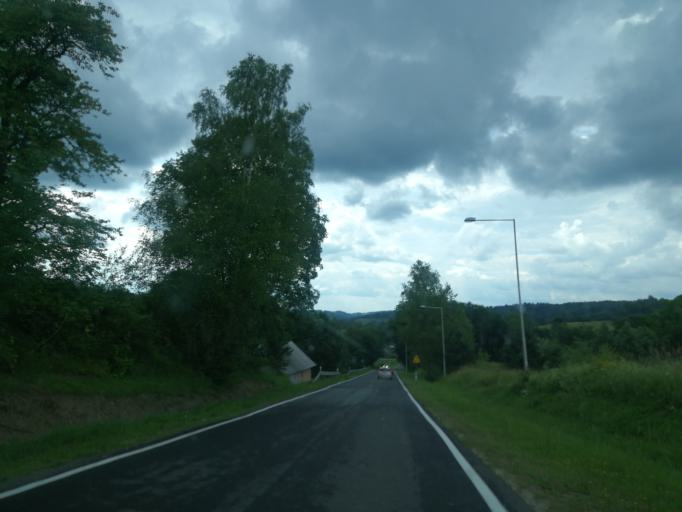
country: PL
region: Subcarpathian Voivodeship
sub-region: Powiat leski
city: Olszanica
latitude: 49.4415
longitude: 22.4524
